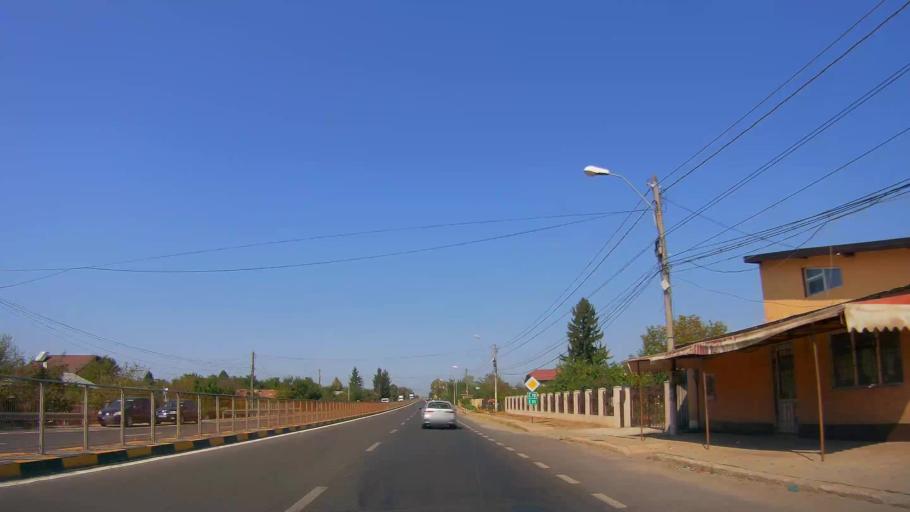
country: RO
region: Giurgiu
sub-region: Comuna Fratesti
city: Remus
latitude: 43.9384
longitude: 25.9778
